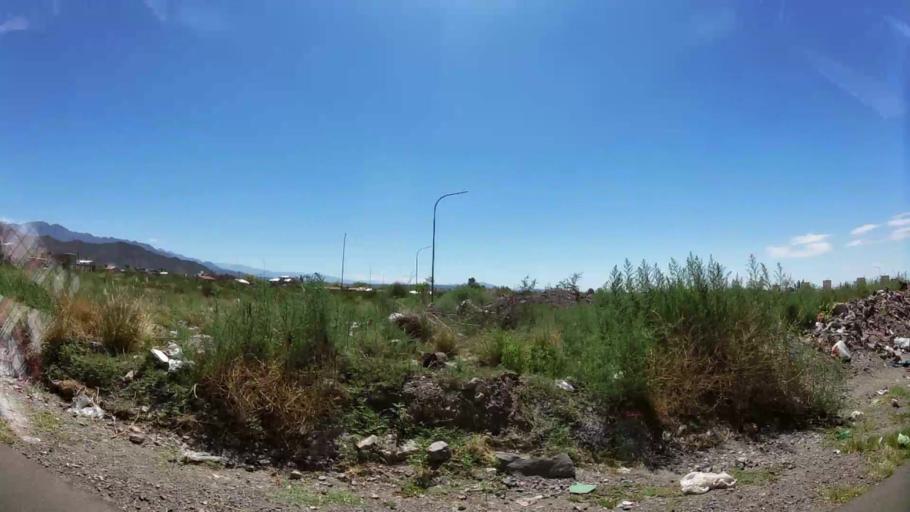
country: AR
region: Mendoza
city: Las Heras
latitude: -32.8498
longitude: -68.8641
